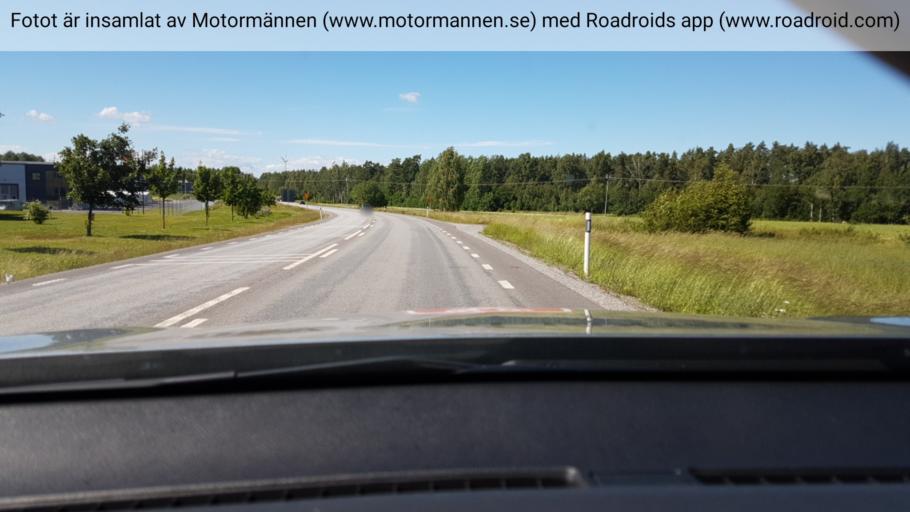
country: SE
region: OErebro
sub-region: Kumla Kommun
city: Kumla
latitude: 59.1521
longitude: 15.1411
